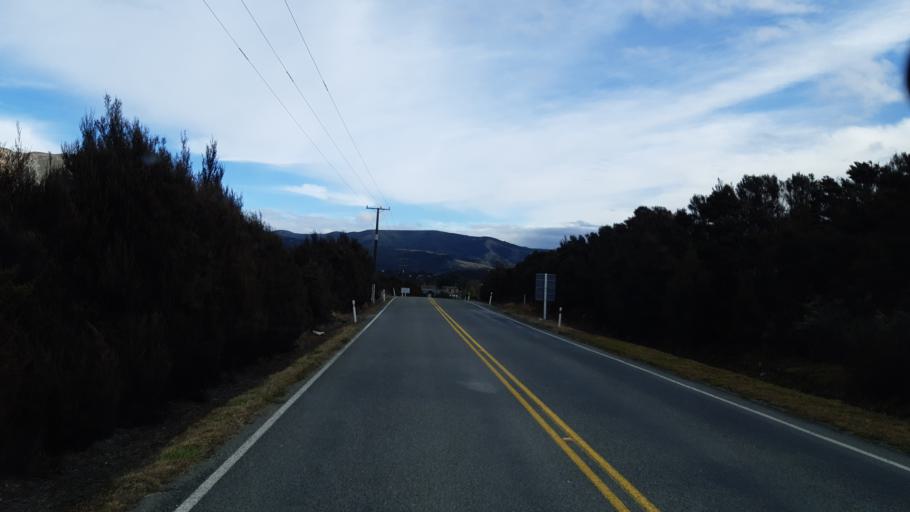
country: NZ
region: Tasman
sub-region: Tasman District
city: Wakefield
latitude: -41.8003
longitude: 172.8603
